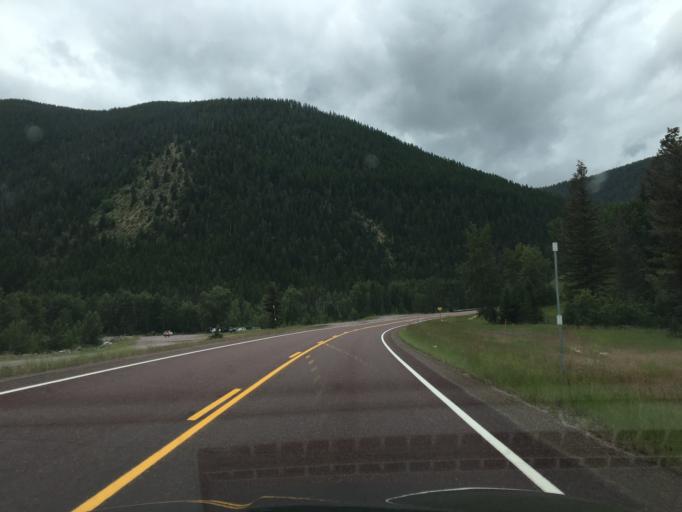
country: US
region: Montana
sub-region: Flathead County
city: Bigfork
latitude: 48.2341
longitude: -113.5636
